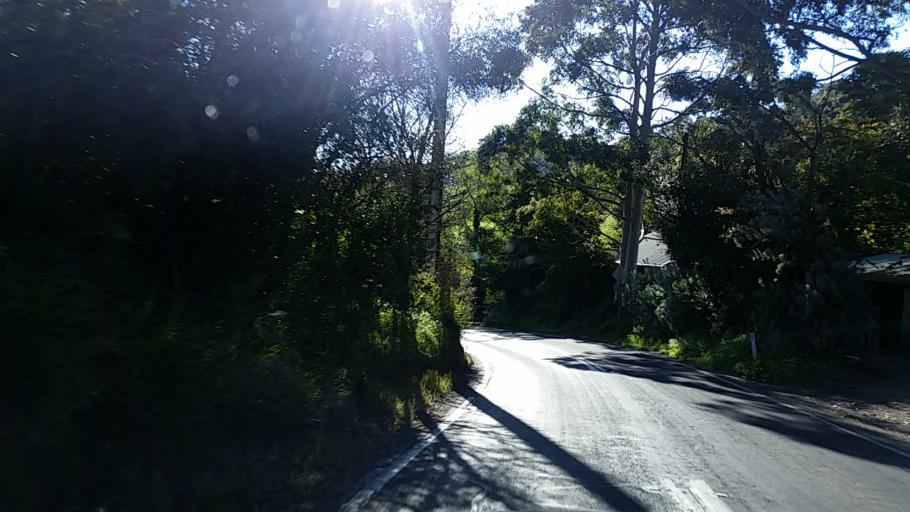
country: AU
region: South Australia
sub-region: Adelaide Hills
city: Adelaide Hills
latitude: -34.9216
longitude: 138.7159
